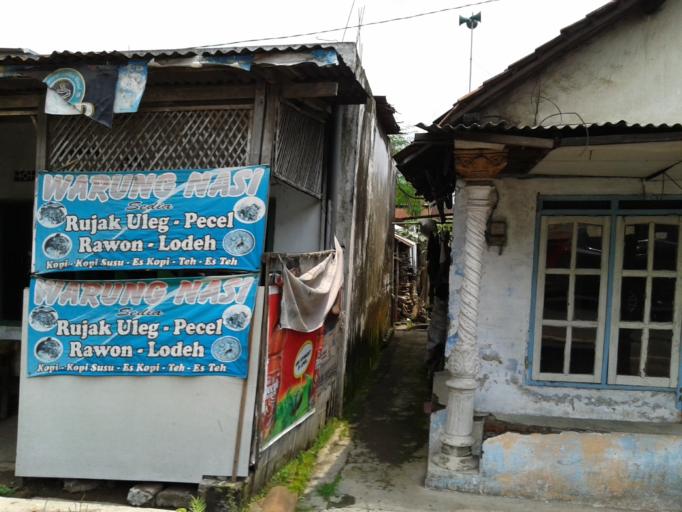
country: ID
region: East Java
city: Singosari
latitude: -7.8710
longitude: 112.6910
